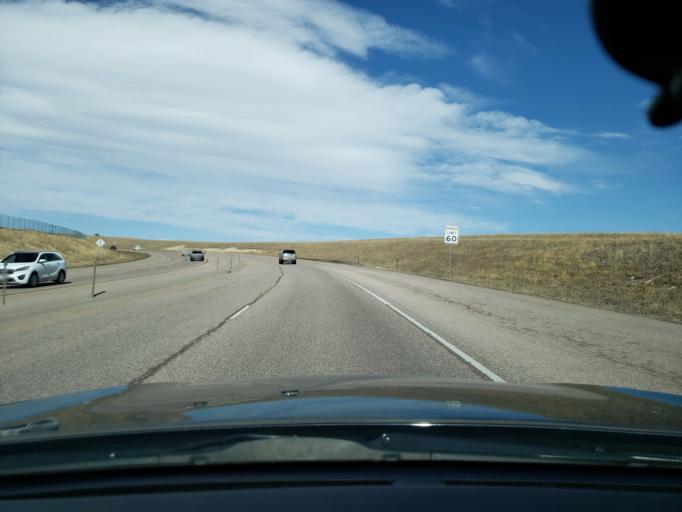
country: US
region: Colorado
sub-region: El Paso County
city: Gleneagle
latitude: 39.0019
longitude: -104.7769
